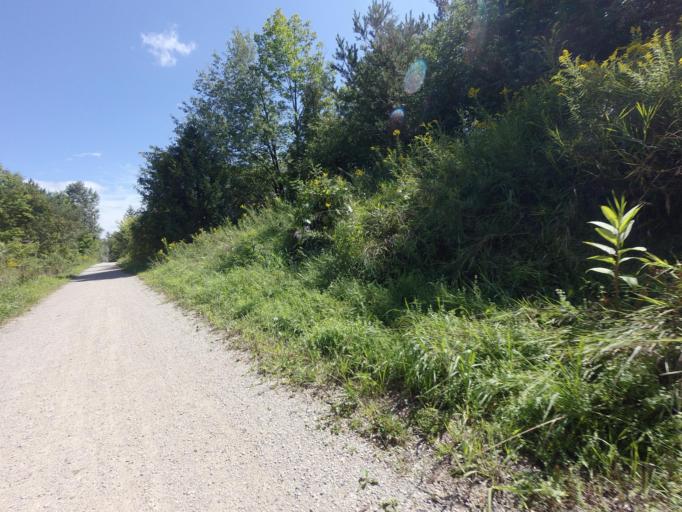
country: CA
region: Ontario
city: Orangeville
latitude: 43.7849
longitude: -80.1409
